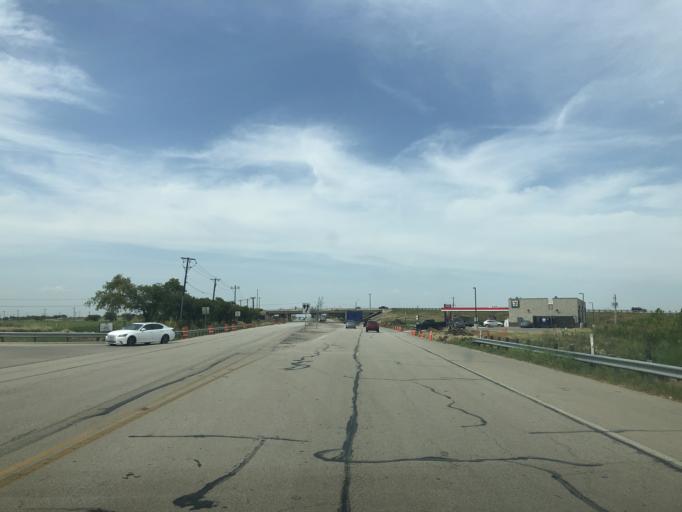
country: US
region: Texas
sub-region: Tarrant County
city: Saginaw
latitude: 32.9127
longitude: -97.3488
